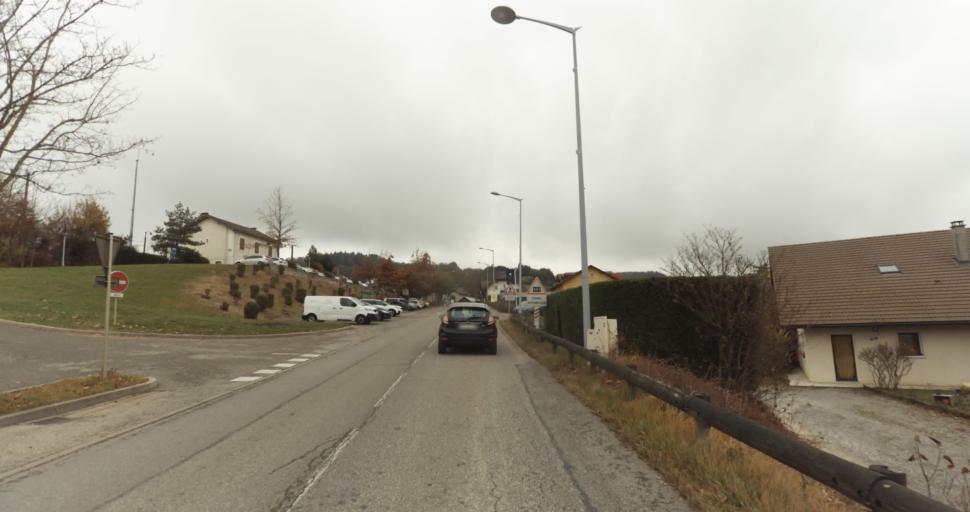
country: FR
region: Rhone-Alpes
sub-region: Departement de la Haute-Savoie
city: Groisy
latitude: 46.0104
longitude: 6.1760
